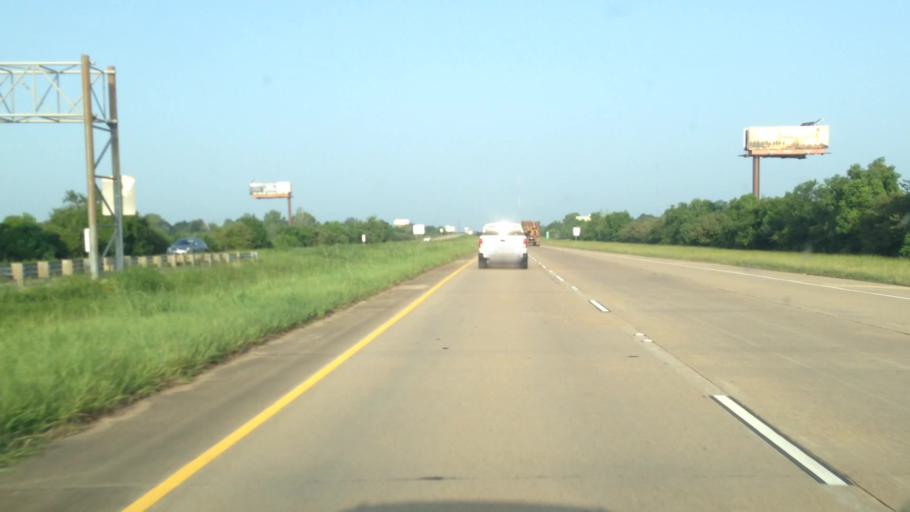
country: US
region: Louisiana
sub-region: Rapides Parish
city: Alexandria
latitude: 31.2399
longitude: -92.4384
